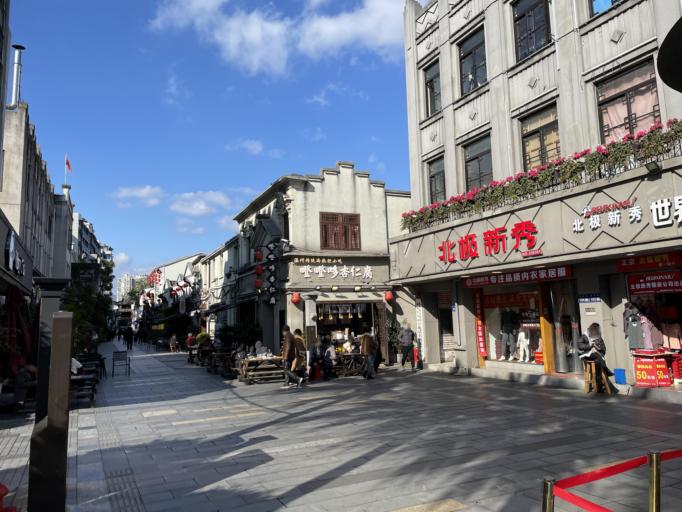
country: CN
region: Zhejiang Sheng
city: Wuma
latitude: 28.0155
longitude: 120.6548
